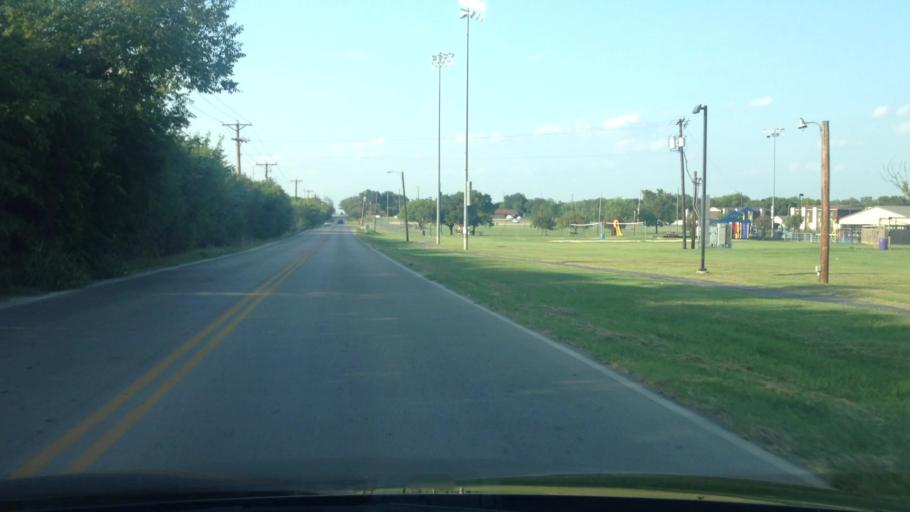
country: US
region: Texas
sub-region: Tarrant County
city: Everman
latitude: 32.6329
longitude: -97.2889
